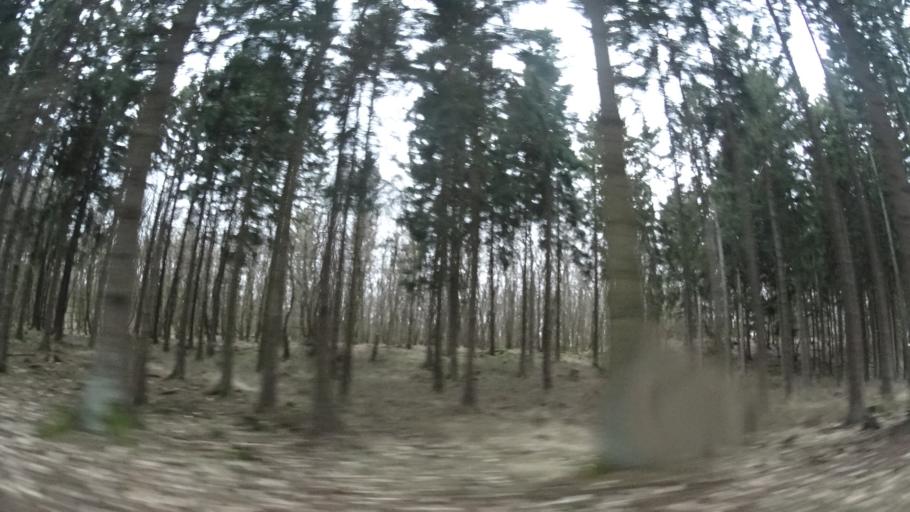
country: DE
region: Rheinland-Pfalz
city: Oberheimbach
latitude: 49.9856
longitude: 7.7813
